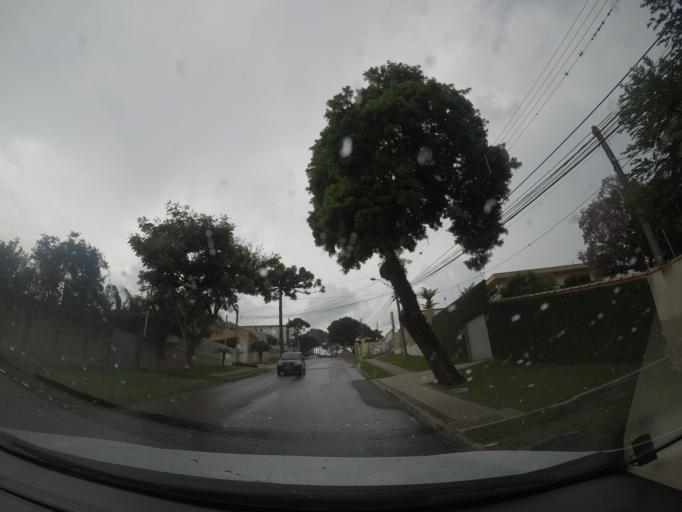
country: BR
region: Parana
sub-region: Sao Jose Dos Pinhais
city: Sao Jose dos Pinhais
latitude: -25.5207
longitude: -49.2571
